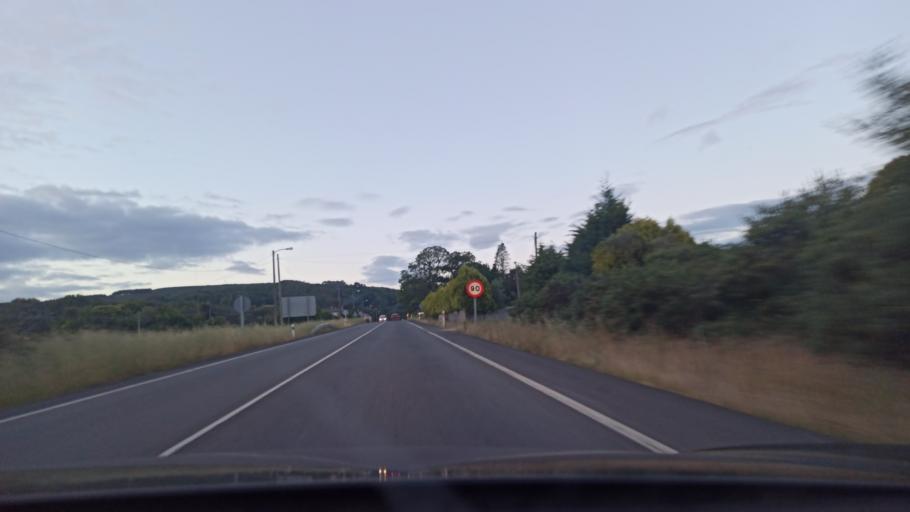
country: ES
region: Galicia
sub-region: Provincia de Lugo
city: Guntin
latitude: 42.9158
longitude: -7.6622
